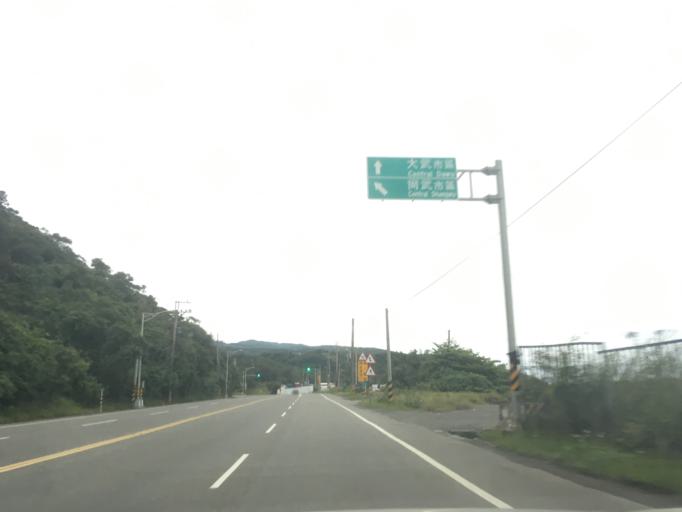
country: TW
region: Taiwan
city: Hengchun
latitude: 22.3351
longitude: 120.8941
